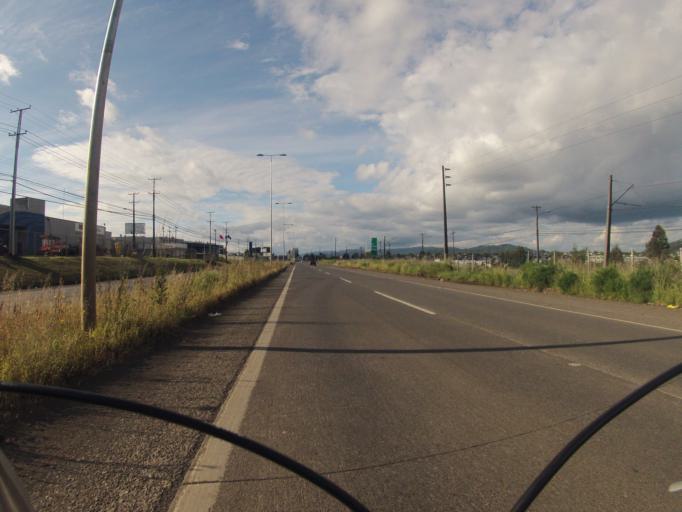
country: CL
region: Araucania
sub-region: Provincia de Cautin
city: Temuco
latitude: -38.7705
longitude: -72.6083
